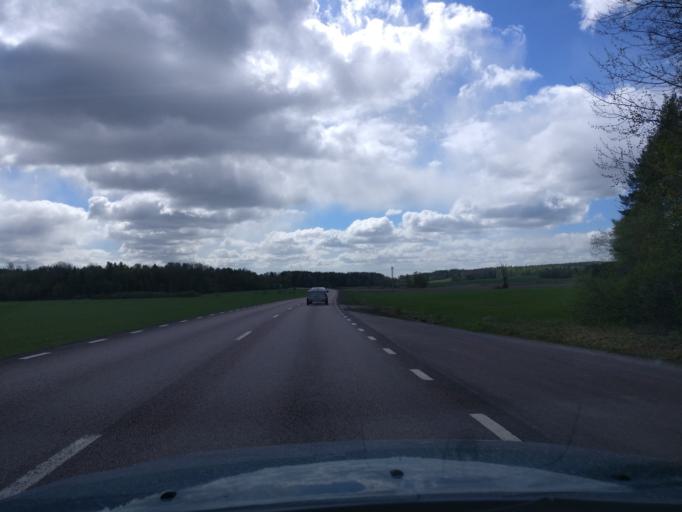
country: SE
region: Vaermland
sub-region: Karlstads Kommun
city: Molkom
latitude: 59.6225
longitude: 13.7304
